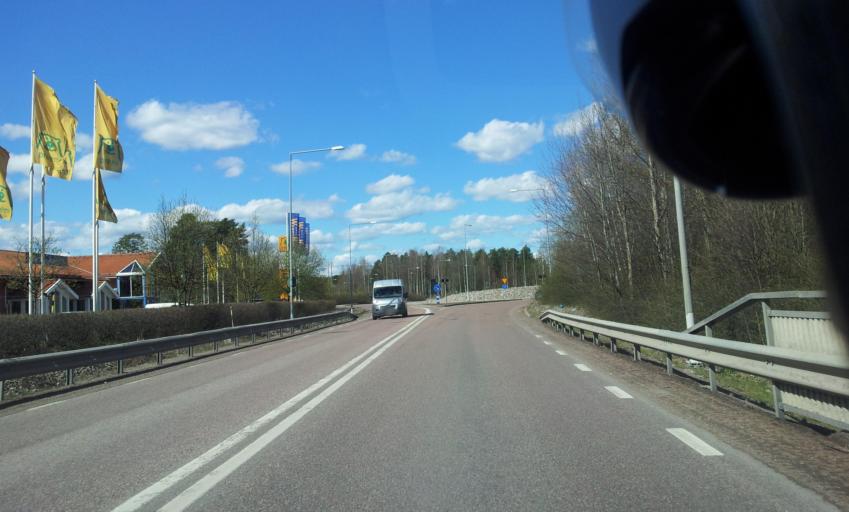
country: SE
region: Dalarna
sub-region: Faluns Kommun
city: Falun
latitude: 60.6246
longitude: 15.6139
